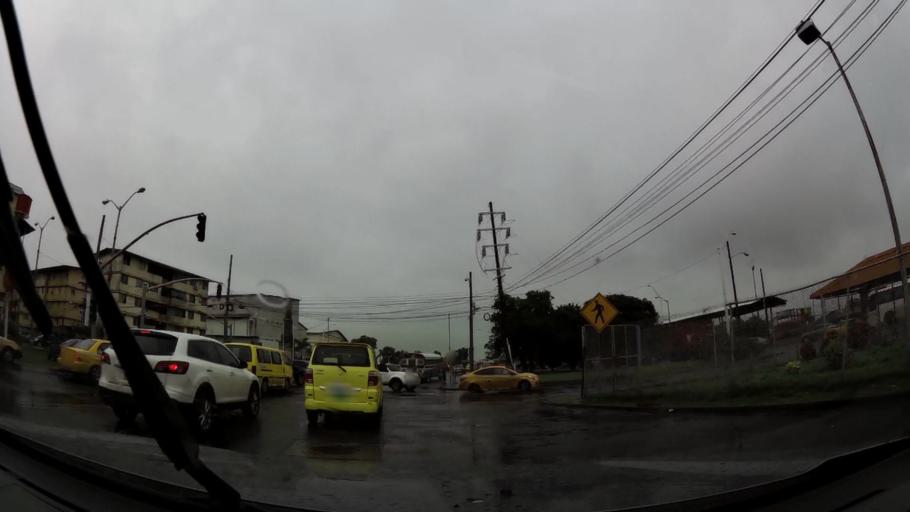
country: PA
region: Colon
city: Colon
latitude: 9.3512
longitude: -79.9000
